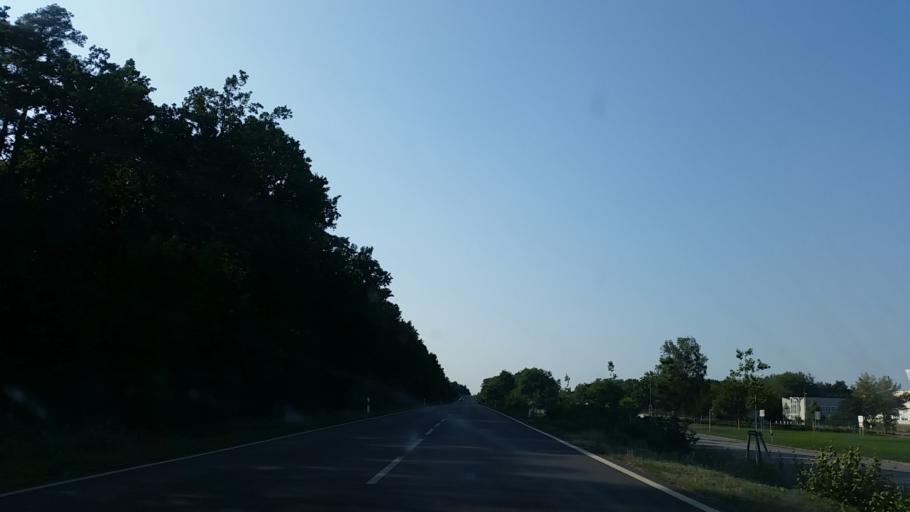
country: DE
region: Brandenburg
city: Meyenburg
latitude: 53.0879
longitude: 14.2264
